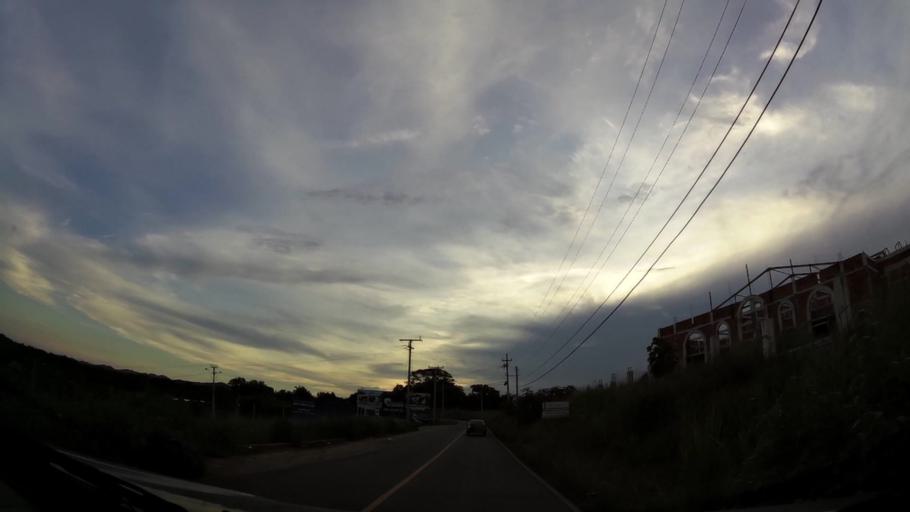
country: PA
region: Panama
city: La Chorrera
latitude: 8.8608
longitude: -79.7669
